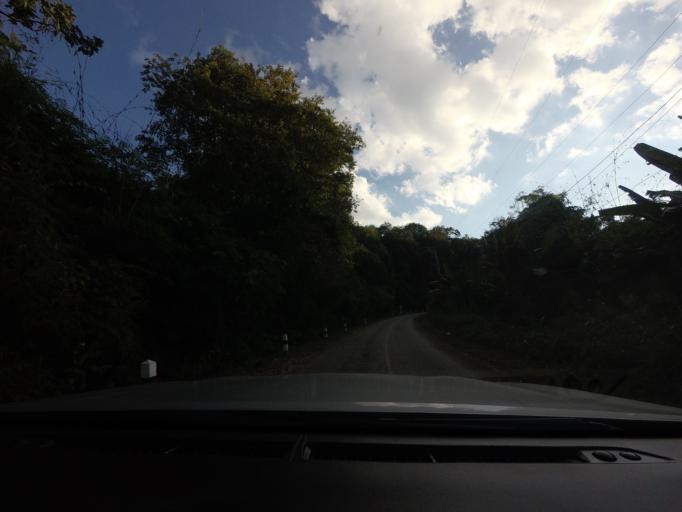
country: TH
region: Chiang Mai
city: Phrao
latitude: 19.5088
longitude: 99.1722
